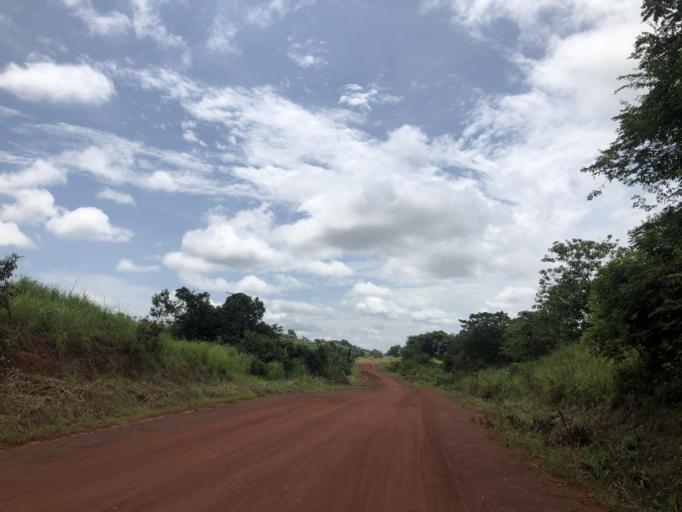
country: SL
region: Northern Province
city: Lunsar
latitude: 8.6702
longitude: -12.5255
